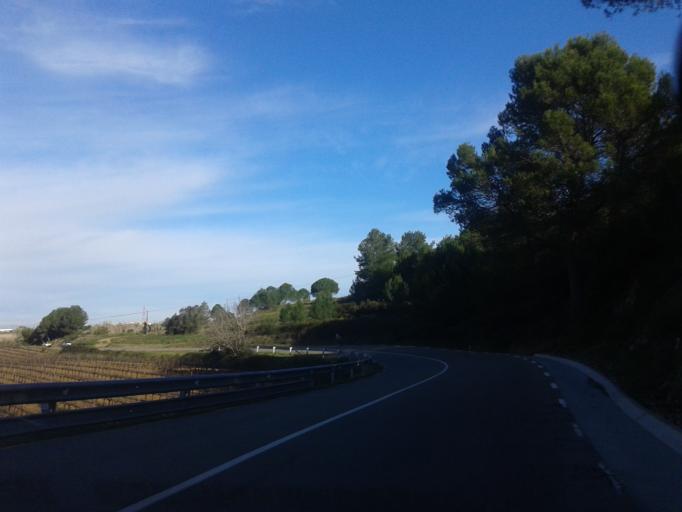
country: ES
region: Catalonia
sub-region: Provincia de Barcelona
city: Avinyonet del Penedes
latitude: 41.3344
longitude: 1.7498
